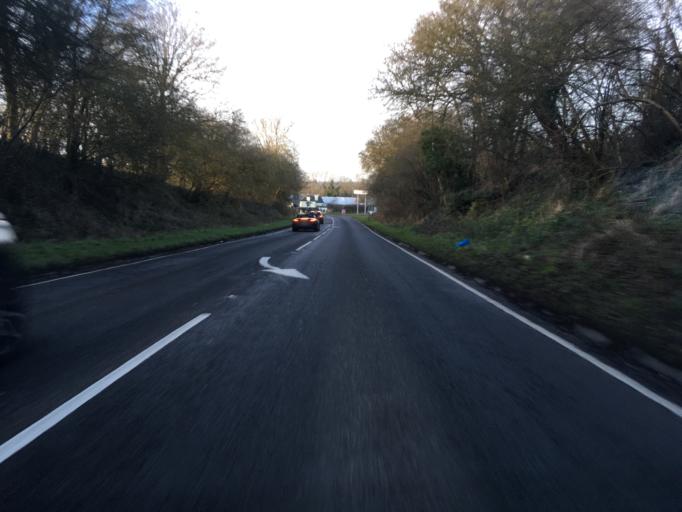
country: GB
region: England
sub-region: Warwickshire
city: Henley in Arden
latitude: 52.2628
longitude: -1.7672
